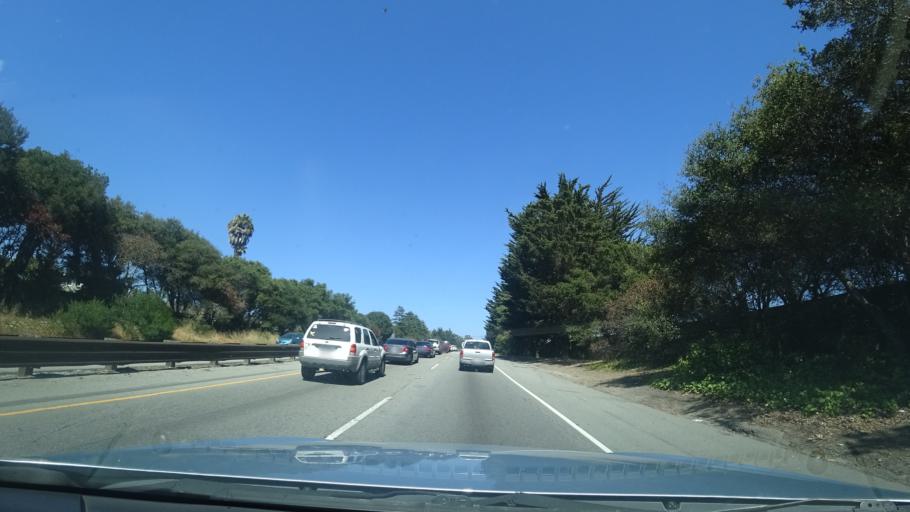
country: US
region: California
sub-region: Santa Cruz County
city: Soquel
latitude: 36.9837
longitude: -121.9512
